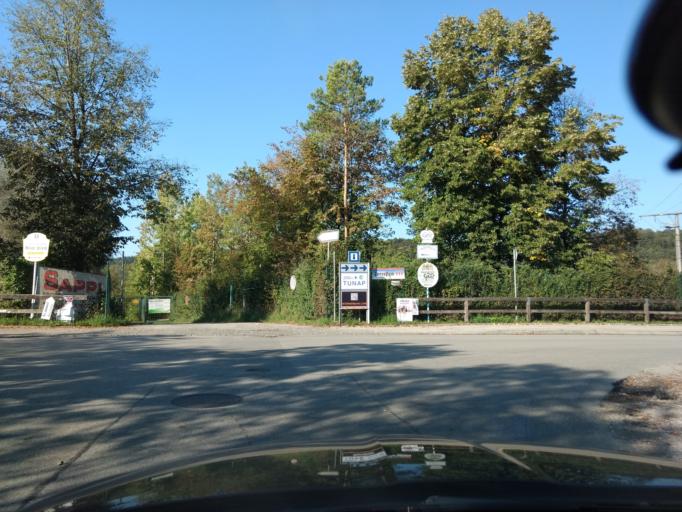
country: DE
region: Bavaria
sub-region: Upper Bavaria
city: Wolfratshausen
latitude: 47.9001
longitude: 11.4233
